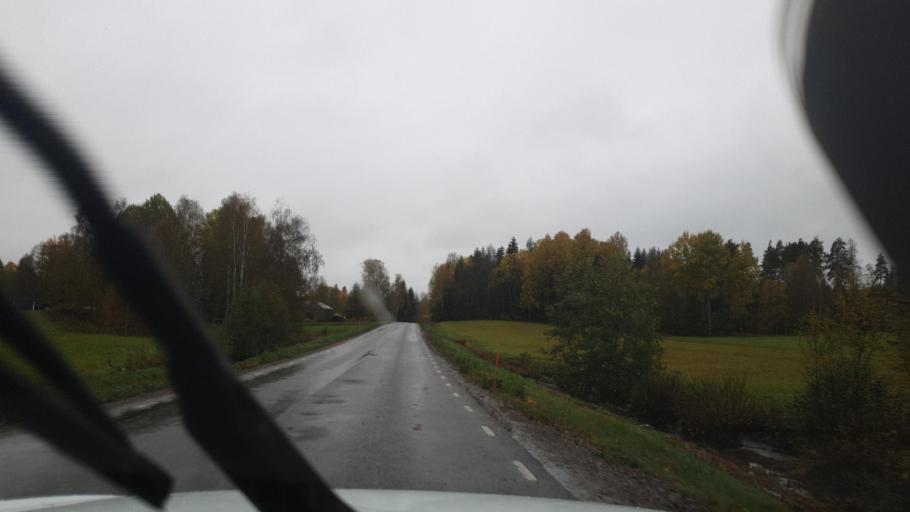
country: SE
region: Vaermland
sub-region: Eda Kommun
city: Charlottenberg
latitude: 59.8040
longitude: 12.1528
